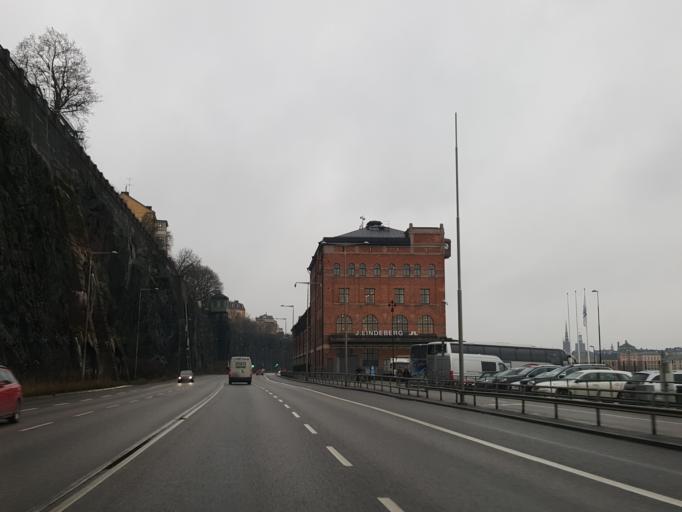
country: SE
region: Stockholm
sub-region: Stockholms Kommun
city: OEstermalm
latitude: 59.3174
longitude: 18.0891
